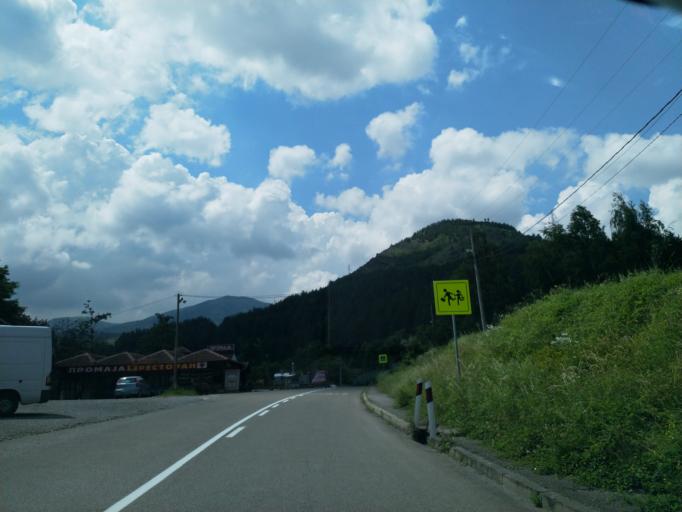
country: RS
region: Central Serbia
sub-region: Rasinski Okrug
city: Aleksandrovac
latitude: 43.3372
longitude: 20.9514
